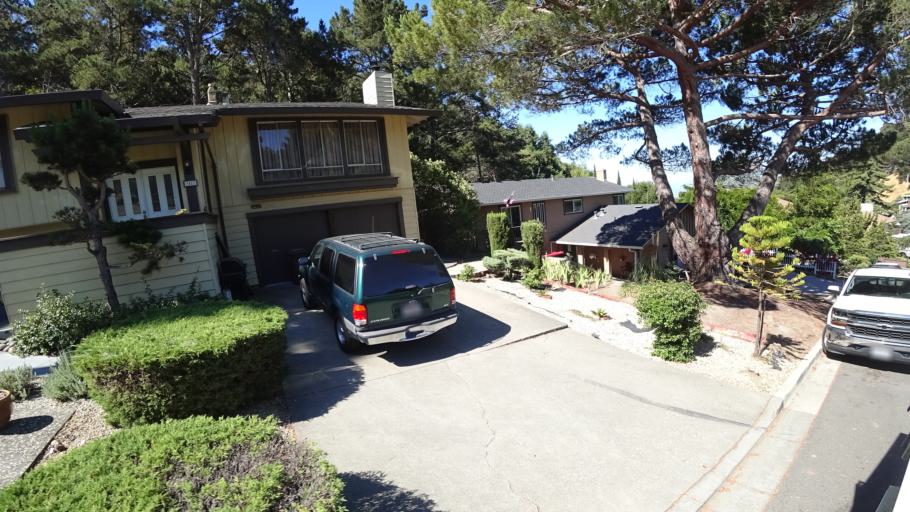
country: US
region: California
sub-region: Alameda County
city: Fairview
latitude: 37.6511
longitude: -122.0325
